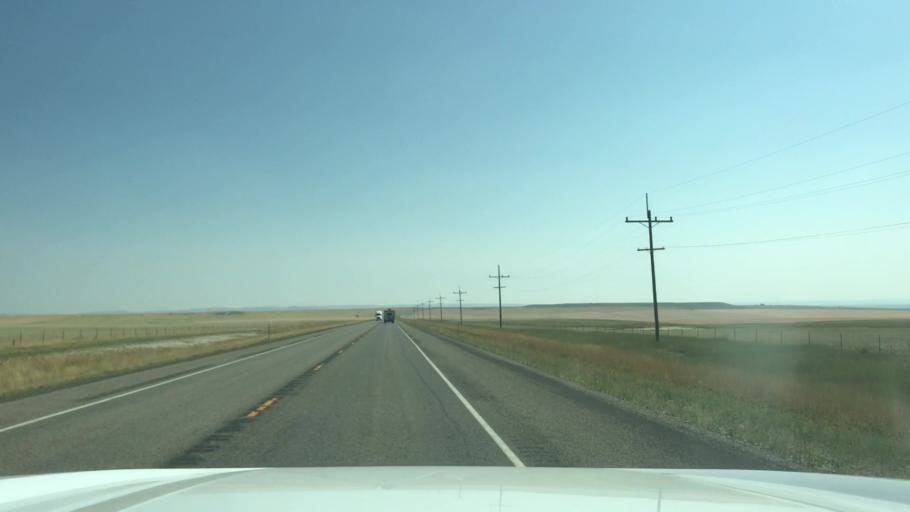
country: US
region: Montana
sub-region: Wheatland County
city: Harlowton
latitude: 46.4995
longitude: -109.7661
